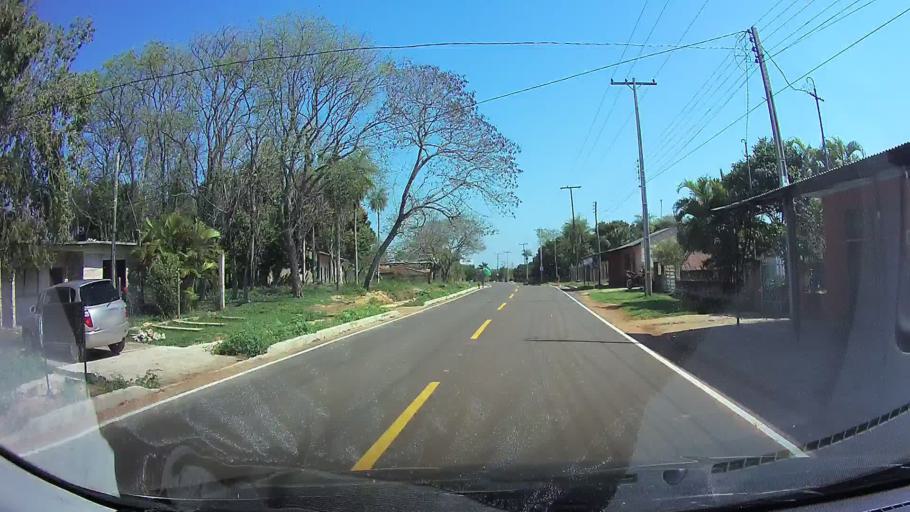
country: PY
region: Central
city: Limpio
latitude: -25.2255
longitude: -57.4882
